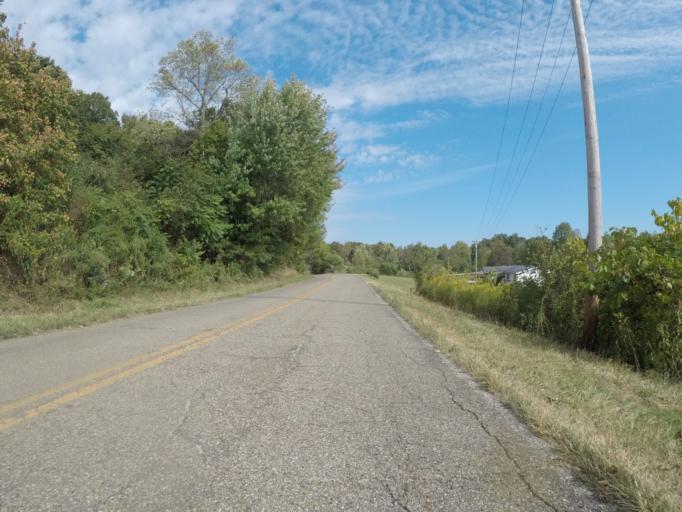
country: US
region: West Virginia
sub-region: Cabell County
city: Lesage
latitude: 38.5749
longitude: -82.4296
